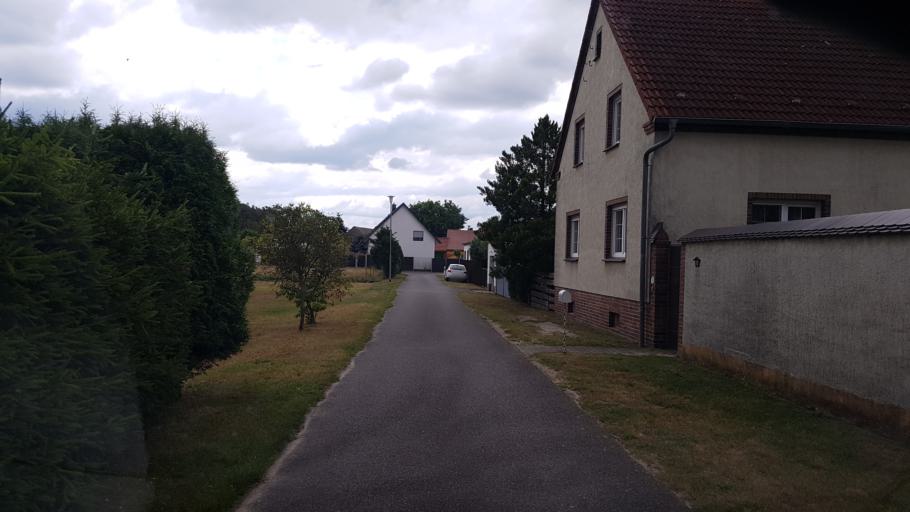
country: DE
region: Brandenburg
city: Crinitz
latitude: 51.7080
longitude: 13.7237
